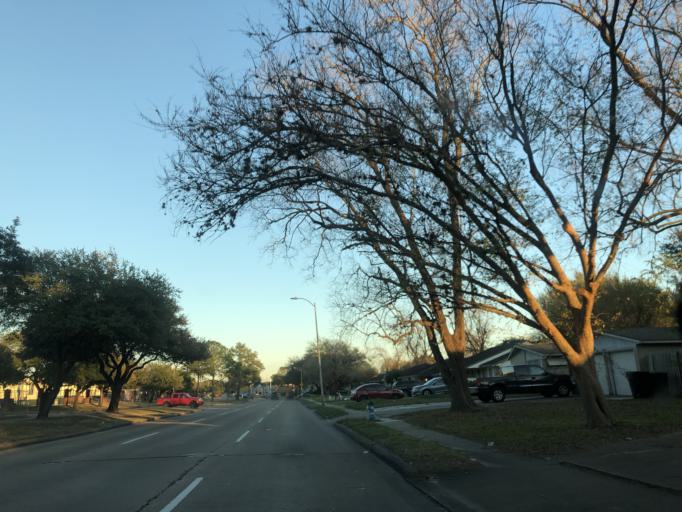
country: US
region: Texas
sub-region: Harris County
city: Bellaire
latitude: 29.6910
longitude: -95.5160
